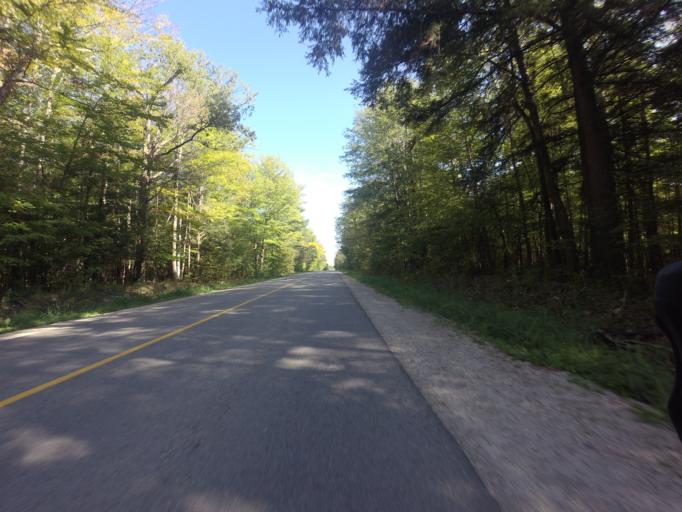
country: CA
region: Ontario
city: Perth
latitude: 44.8966
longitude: -76.3259
